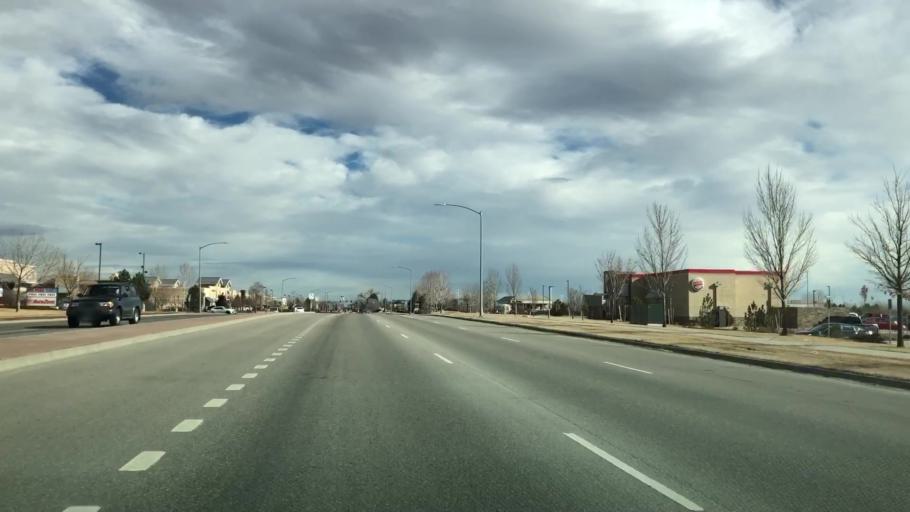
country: US
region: Colorado
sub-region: Weld County
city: Windsor
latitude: 40.4795
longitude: -104.9325
